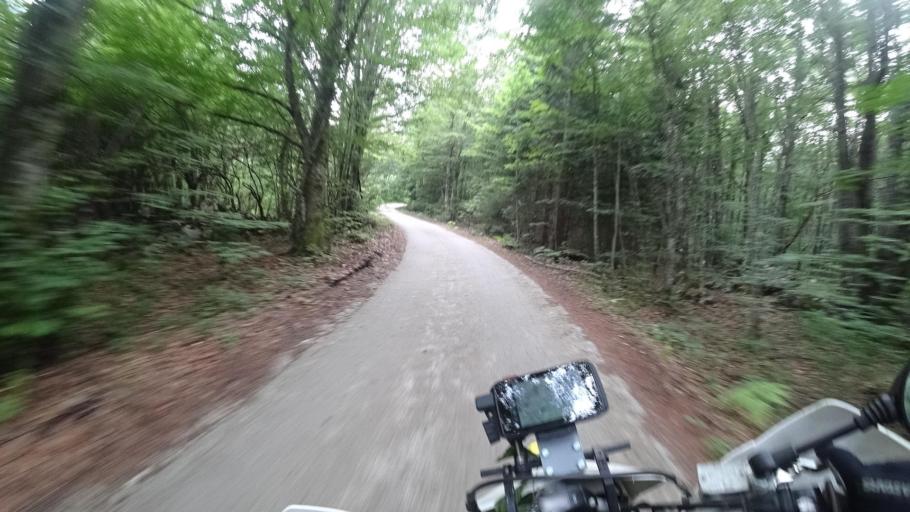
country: HR
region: Licko-Senjska
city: Jezerce
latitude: 44.9037
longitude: 15.5998
